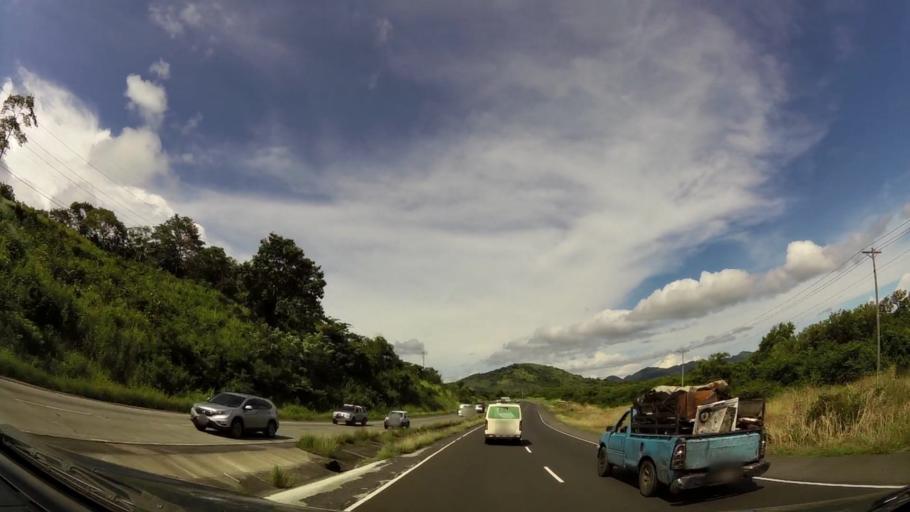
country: PA
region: Panama
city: Bejuco
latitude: 8.6542
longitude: -79.8719
